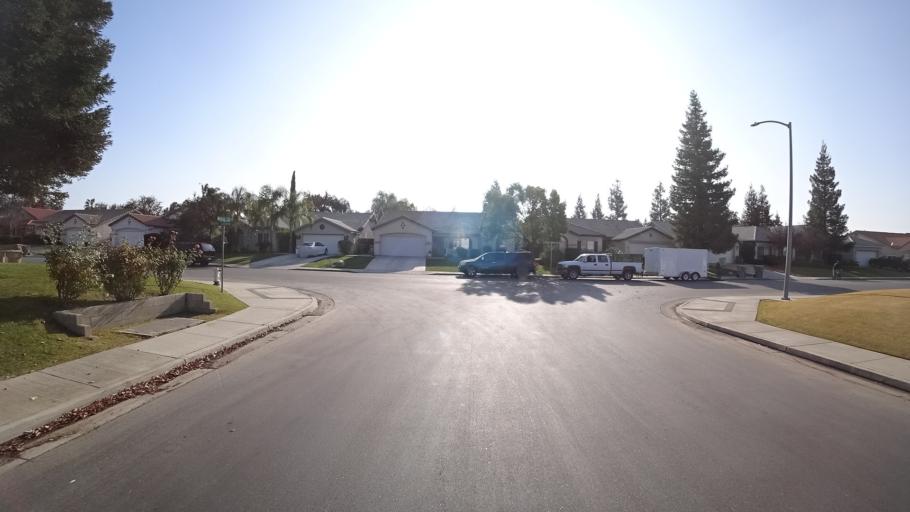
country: US
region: California
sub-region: Kern County
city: Greenacres
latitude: 35.4139
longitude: -119.0964
